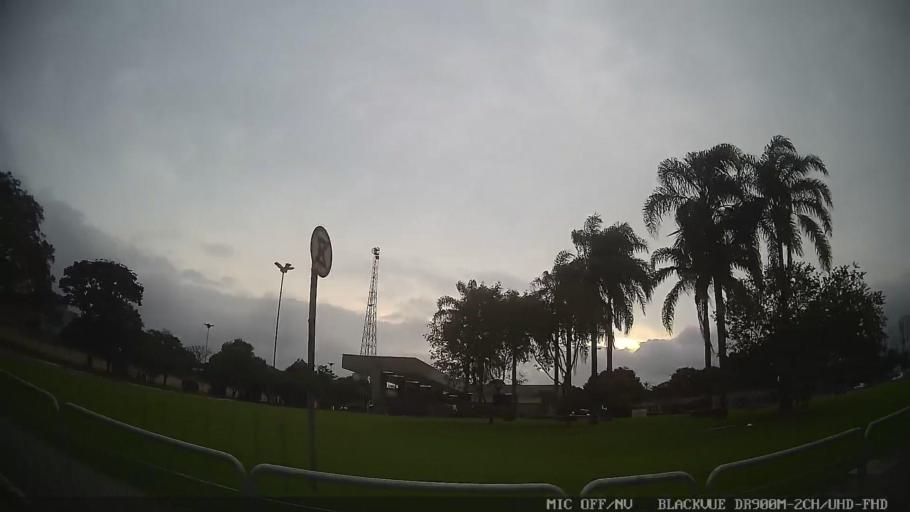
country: BR
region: Sao Paulo
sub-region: Mogi das Cruzes
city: Mogi das Cruzes
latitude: -23.5120
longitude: -46.1861
